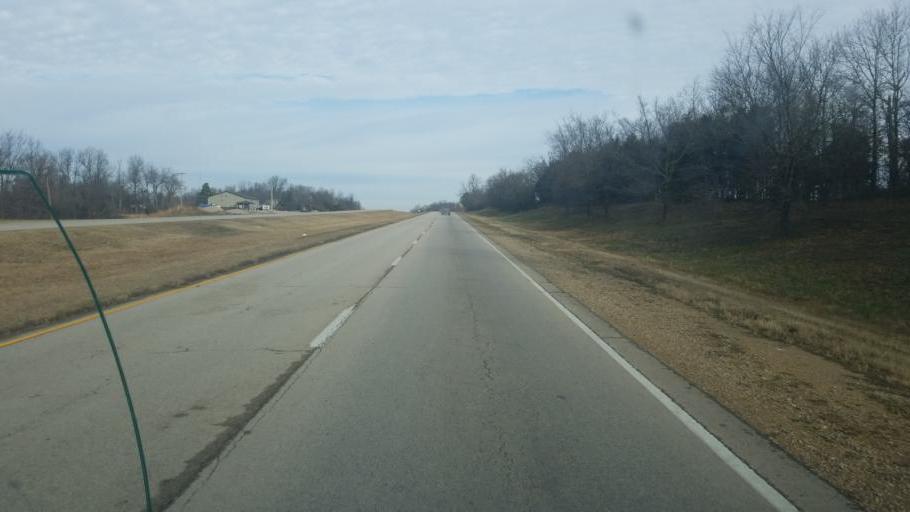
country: US
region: Missouri
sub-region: Stoddard County
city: Dexter
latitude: 36.8287
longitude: -89.9413
